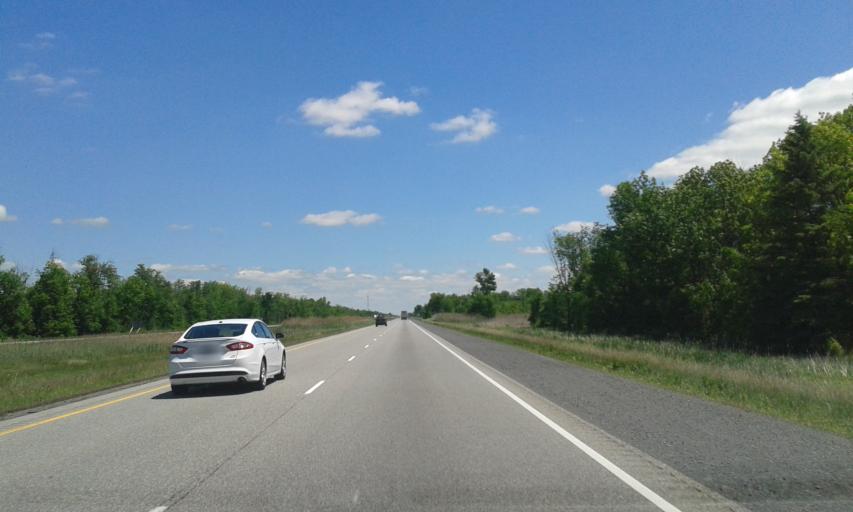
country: US
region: New York
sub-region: St. Lawrence County
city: Massena
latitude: 44.9940
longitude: -75.0401
